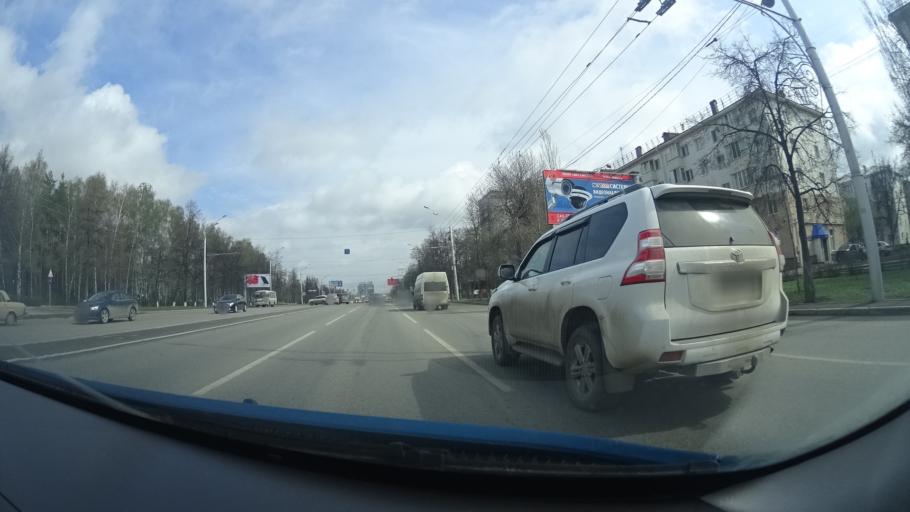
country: RU
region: Bashkortostan
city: Ufa
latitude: 54.7687
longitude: 56.0214
